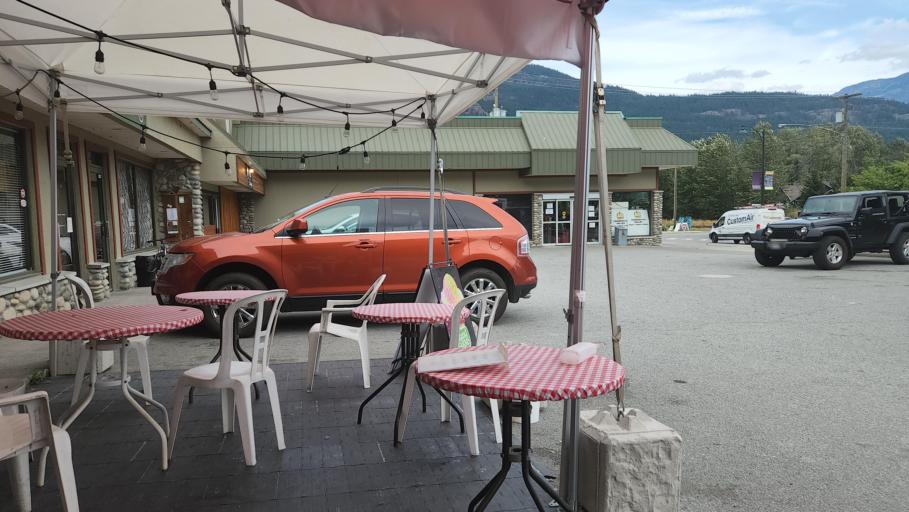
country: CA
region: British Columbia
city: Pemberton
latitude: 50.3218
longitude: -122.8068
